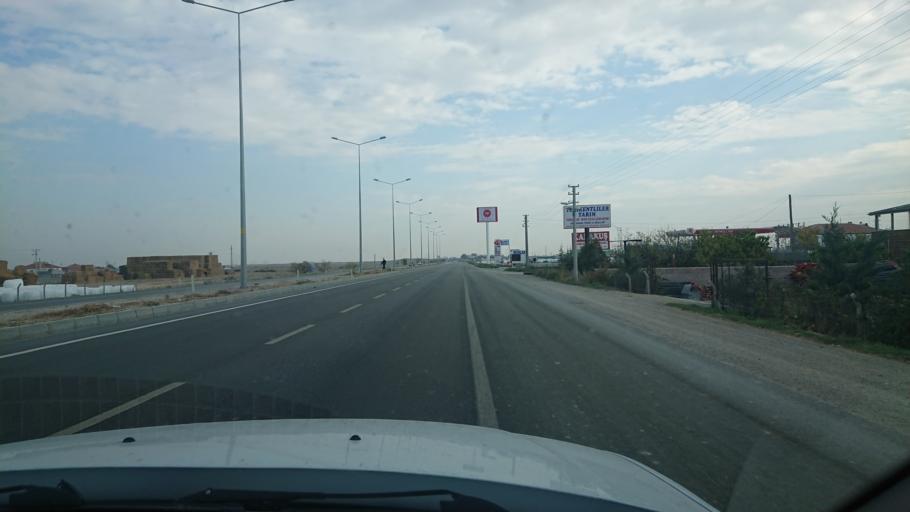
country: TR
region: Aksaray
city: Yesilova
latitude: 38.2923
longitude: 33.7657
